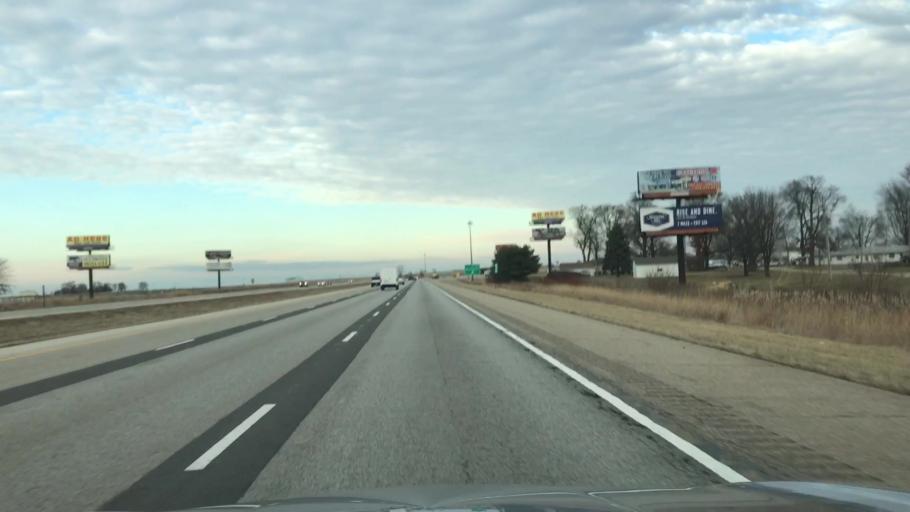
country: US
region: Illinois
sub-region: Logan County
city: Lincoln
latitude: 40.0671
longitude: -89.4469
